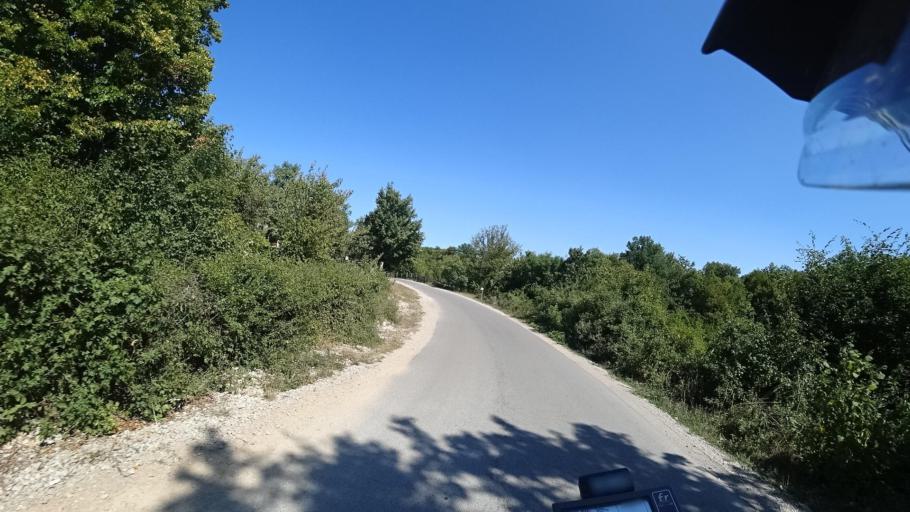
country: HR
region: Licko-Senjska
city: Otocac
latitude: 44.7281
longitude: 15.3135
